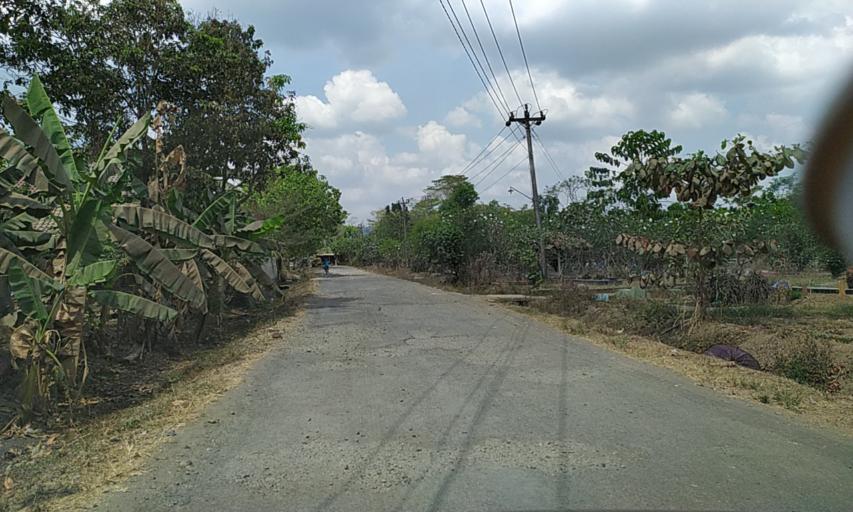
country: ID
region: Central Java
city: Cigintung
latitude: -7.3689
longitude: 108.8041
